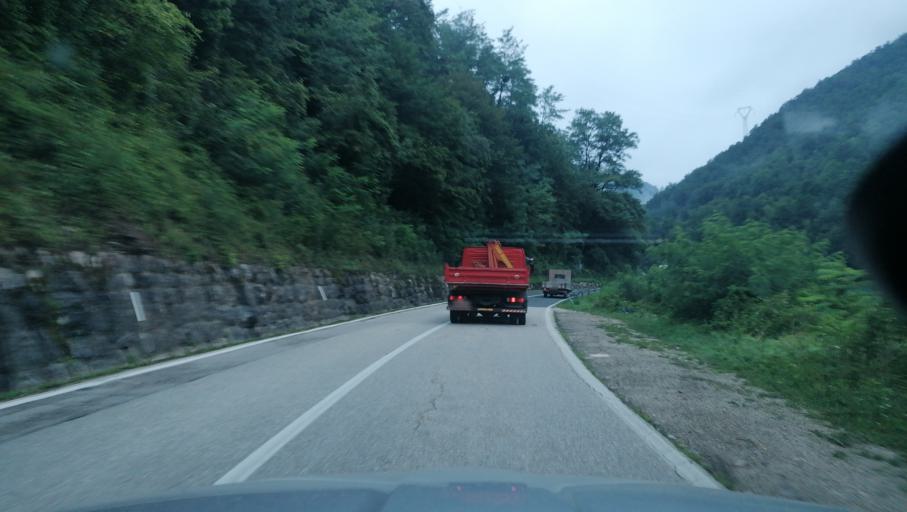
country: BA
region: Federation of Bosnia and Herzegovina
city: Jablanica
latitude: 43.7312
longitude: 17.6817
